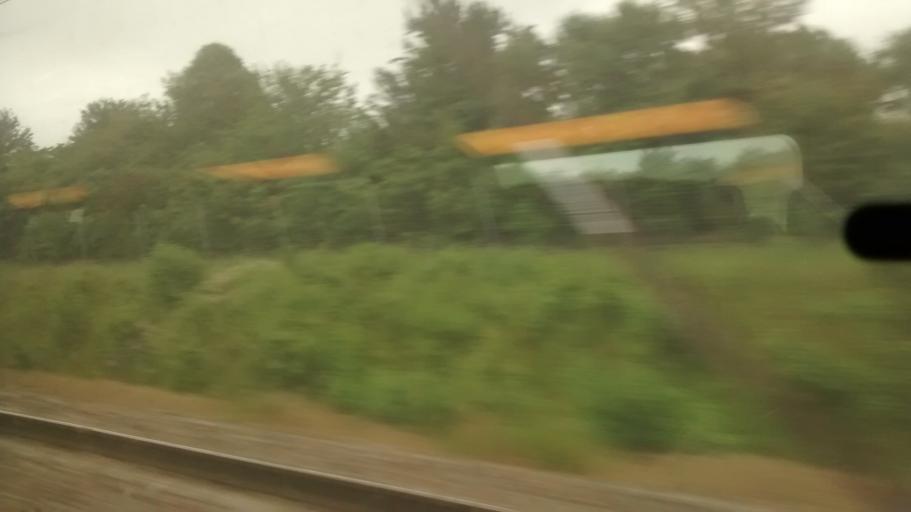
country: FR
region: Bourgogne
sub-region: Departement de l'Yonne
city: Vinneuf
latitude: 48.3705
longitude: 3.1147
